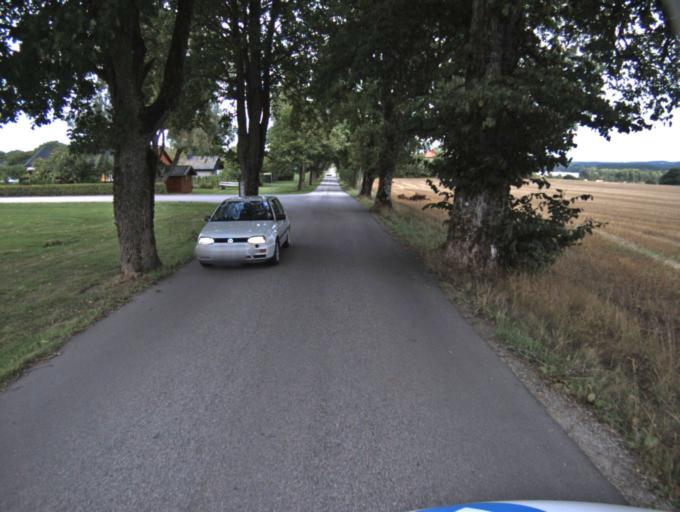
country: SE
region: Vaestra Goetaland
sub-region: Ulricehamns Kommun
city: Ulricehamn
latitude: 57.8373
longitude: 13.2907
